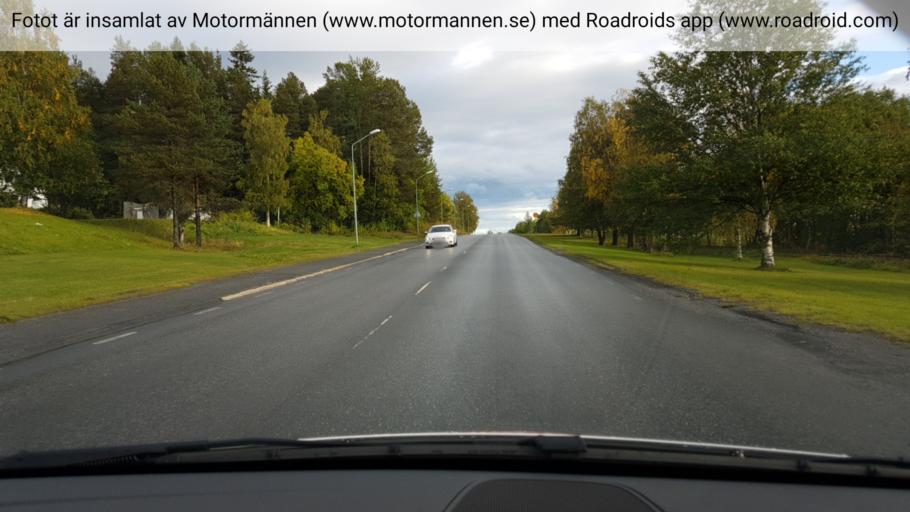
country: SE
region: Jaemtland
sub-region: Are Kommun
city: Jarpen
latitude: 63.3497
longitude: 13.4529
